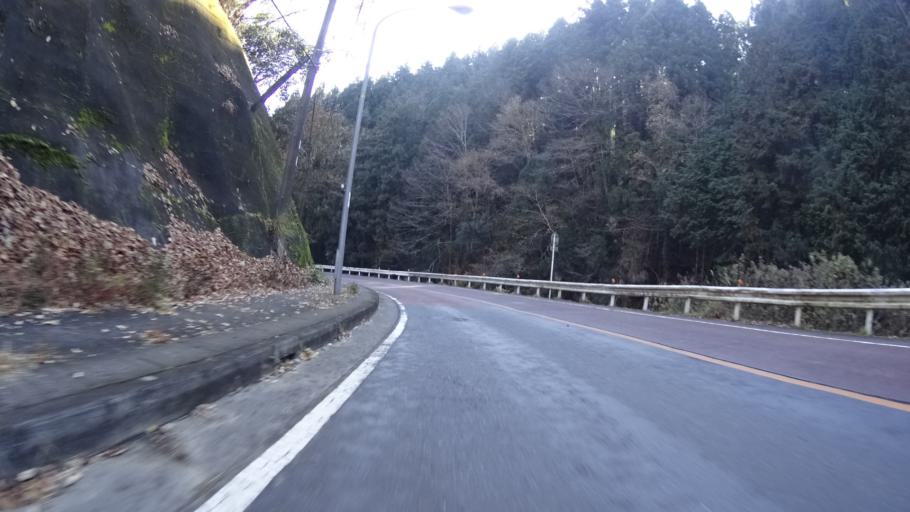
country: JP
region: Yamanashi
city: Uenohara
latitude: 35.6302
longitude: 139.1447
